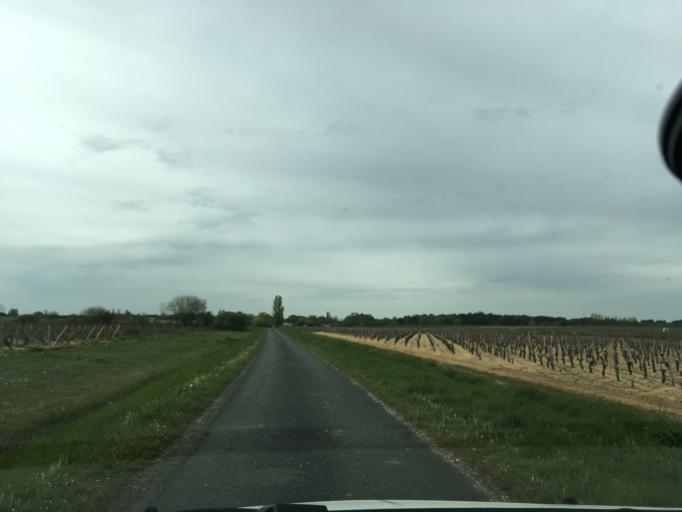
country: FR
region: Aquitaine
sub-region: Departement de la Gironde
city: Lesparre-Medoc
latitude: 45.3203
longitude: -0.8952
